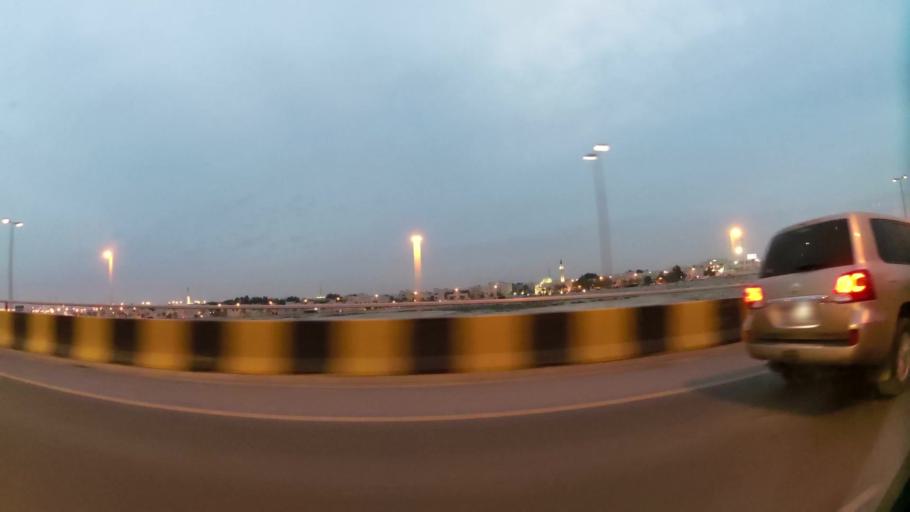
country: BH
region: Northern
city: Madinat `Isa
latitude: 26.1746
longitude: 50.5414
